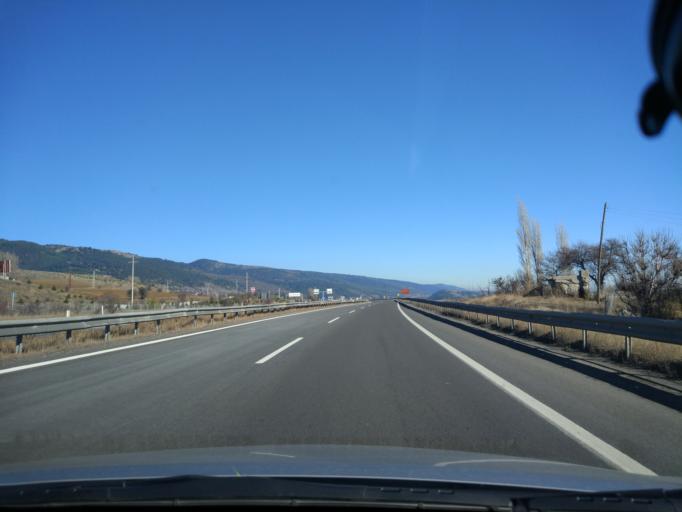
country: TR
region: Bolu
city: Gerede
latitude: 40.7990
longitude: 32.2389
